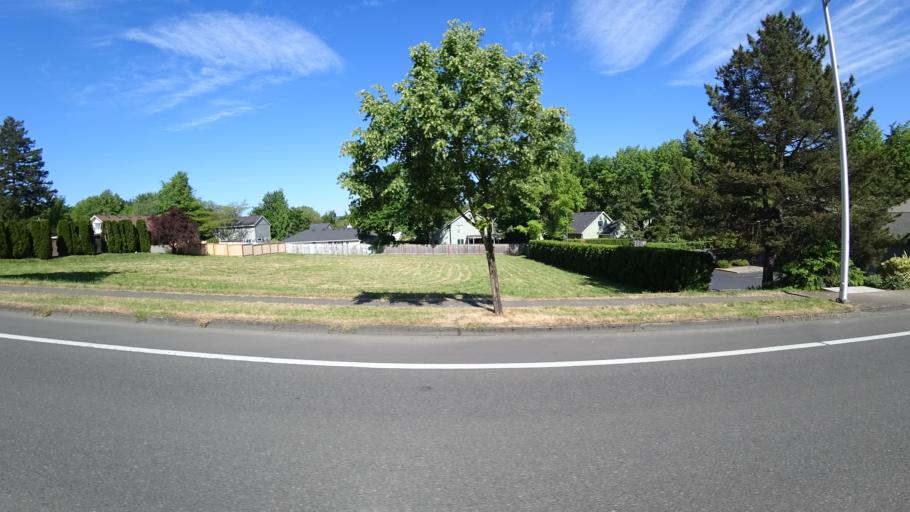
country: US
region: Oregon
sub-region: Washington County
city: Beaverton
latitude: 45.4651
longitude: -122.8037
